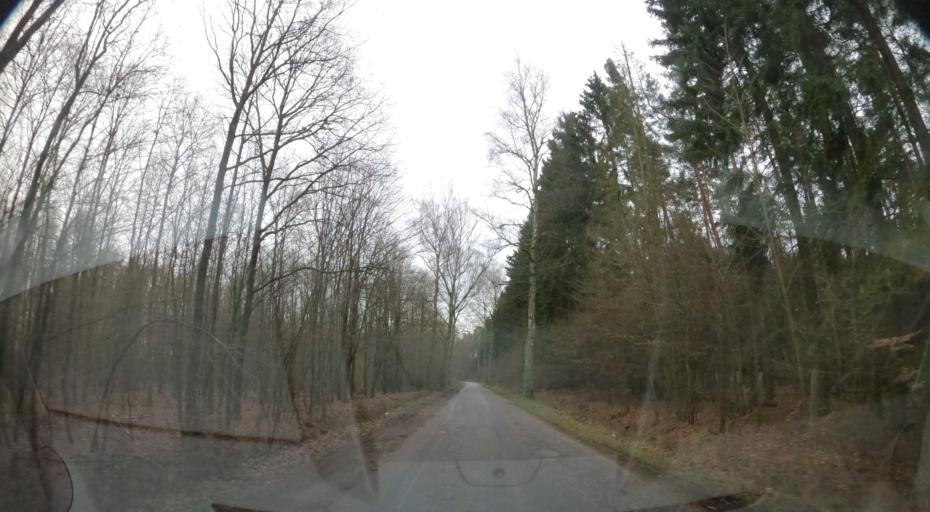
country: PL
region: Greater Poland Voivodeship
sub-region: Powiat zlotowski
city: Krajenka
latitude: 53.2832
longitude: 17.0734
